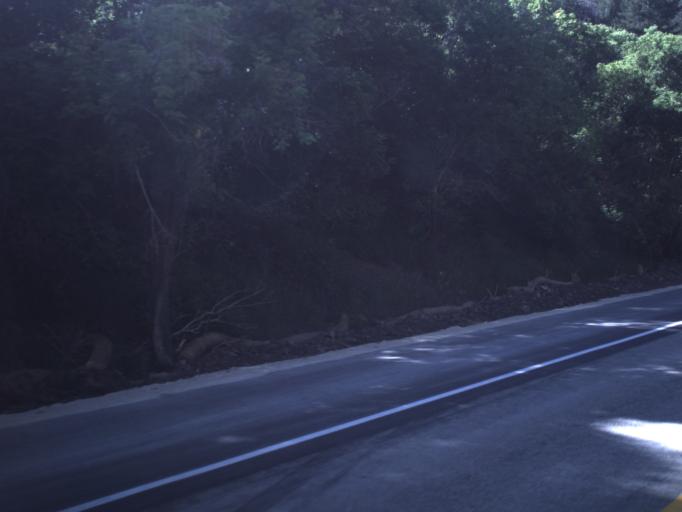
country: US
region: Utah
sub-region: Wasatch County
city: Heber
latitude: 40.3841
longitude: -111.3015
